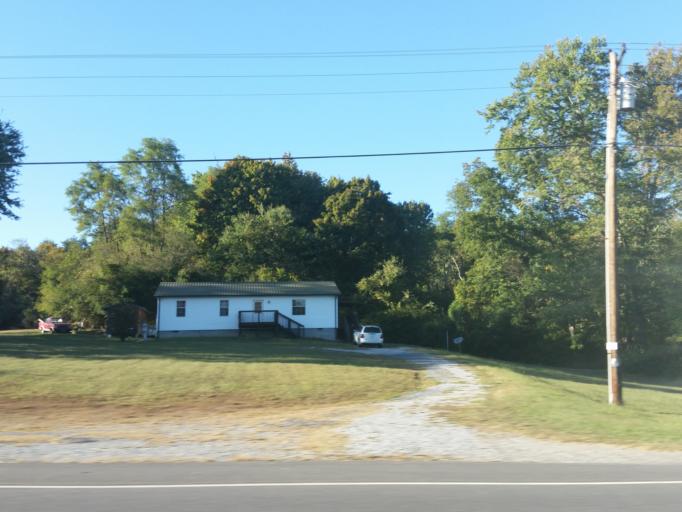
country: US
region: Tennessee
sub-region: Grainger County
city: Bean Station
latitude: 36.3363
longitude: -83.3505
